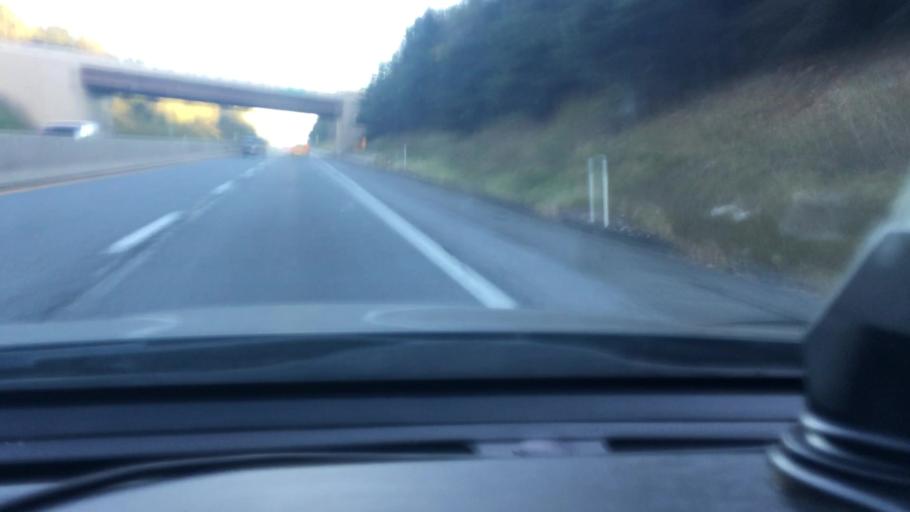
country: US
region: Pennsylvania
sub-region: Carbon County
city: Towamensing Trails
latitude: 40.9378
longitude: -75.6409
